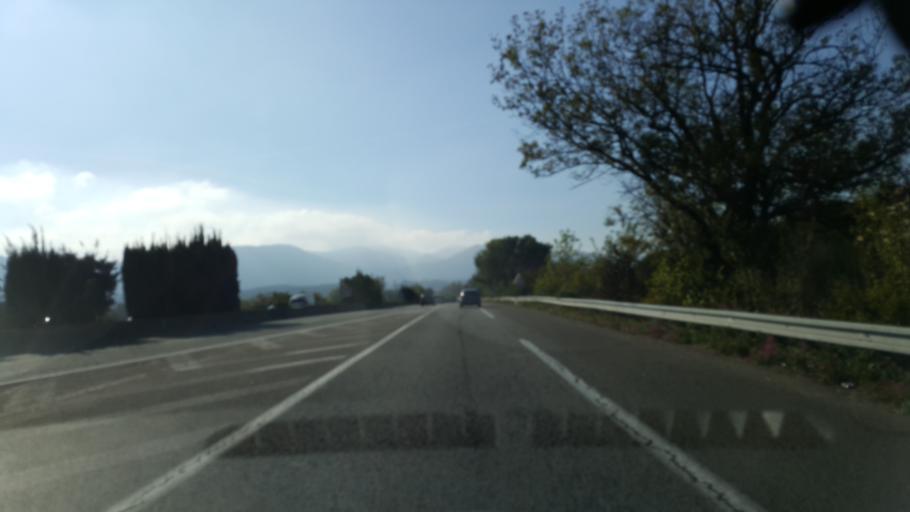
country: FR
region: Provence-Alpes-Cote d'Azur
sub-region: Departement des Bouches-du-Rhone
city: Aubagne
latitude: 43.2898
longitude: 5.5520
